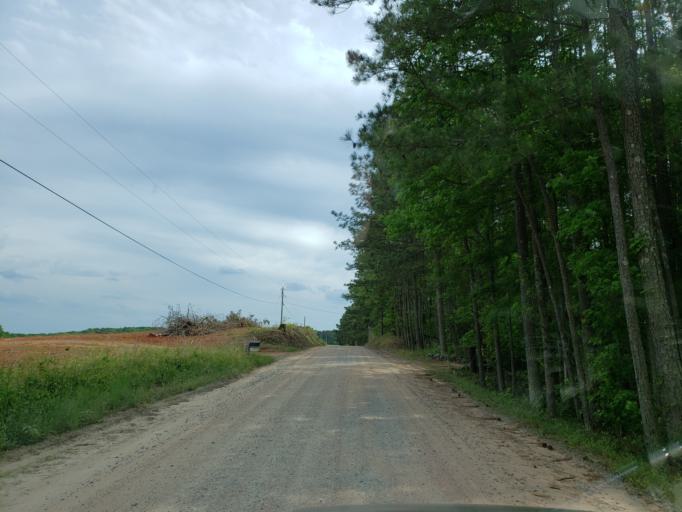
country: US
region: Georgia
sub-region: Monroe County
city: Forsyth
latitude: 32.9800
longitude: -83.9136
